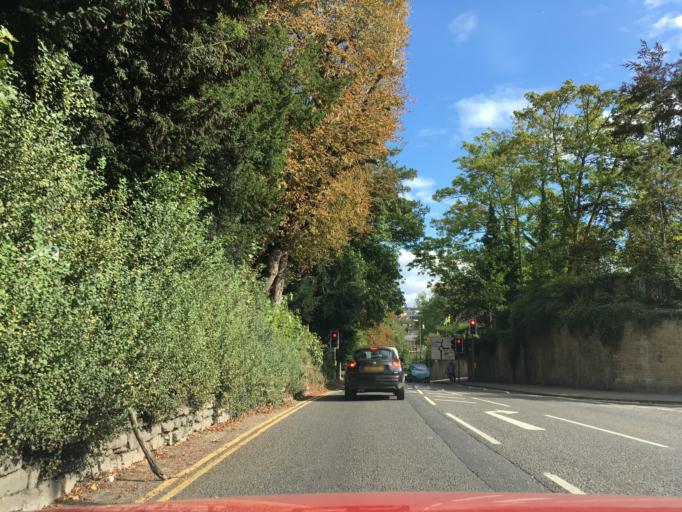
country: GB
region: England
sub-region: Gloucestershire
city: Stroud
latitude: 51.7482
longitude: -2.2195
